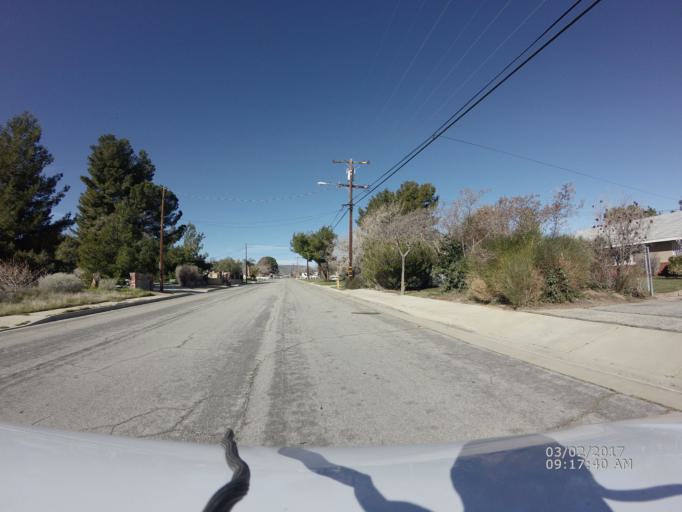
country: US
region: California
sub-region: Los Angeles County
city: Quartz Hill
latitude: 34.6345
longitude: -118.2139
